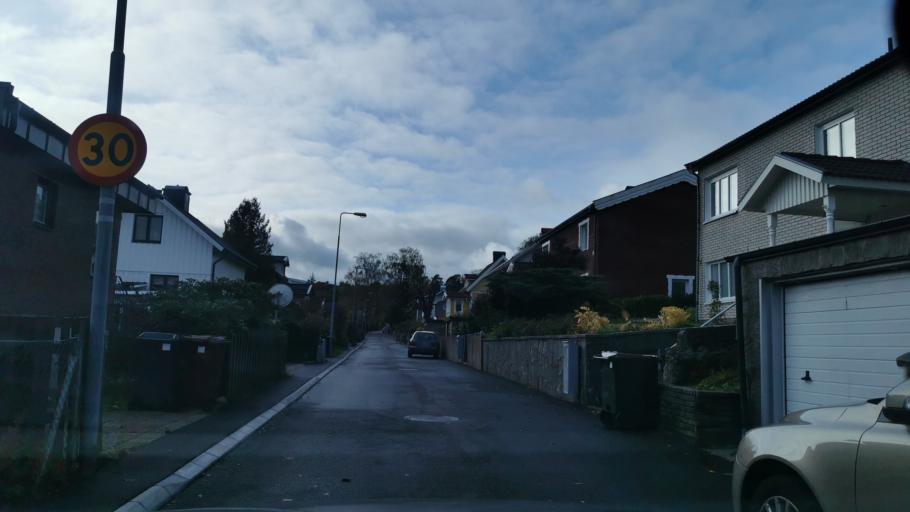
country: SE
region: Vaestra Goetaland
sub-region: Partille Kommun
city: Partille
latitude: 57.7265
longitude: 12.0796
